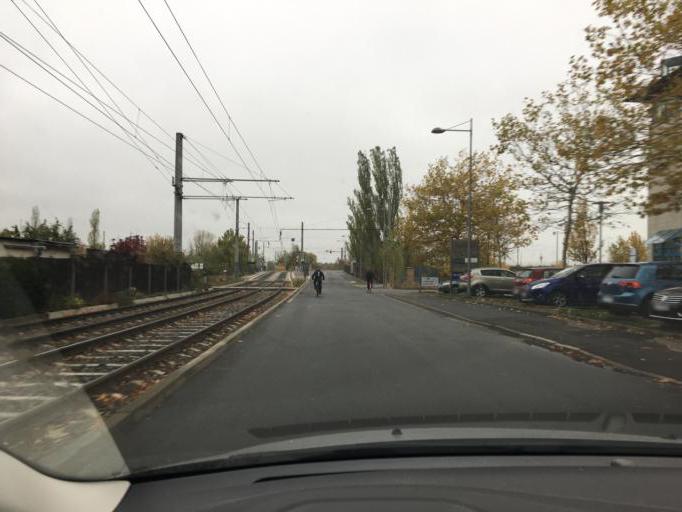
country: DE
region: Saxony
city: Leipzig
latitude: 51.3187
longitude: 12.3175
